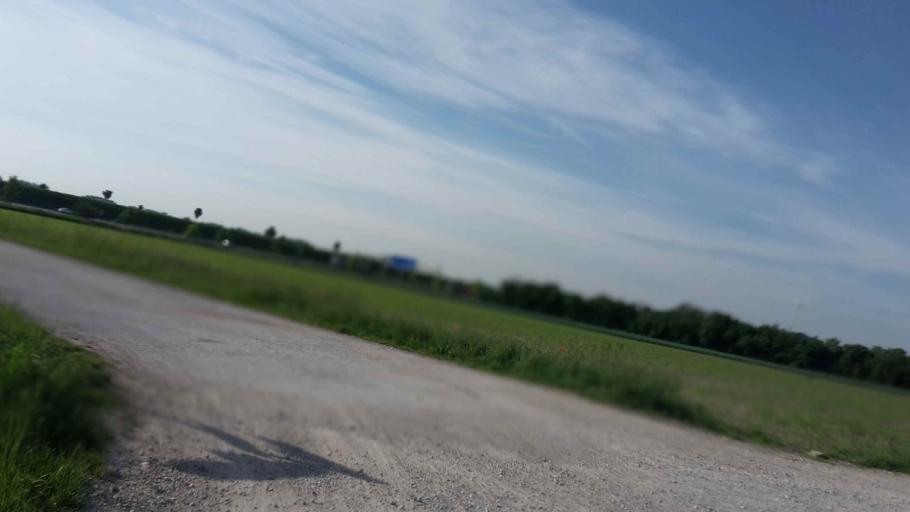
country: DE
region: Bavaria
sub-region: Upper Bavaria
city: Garching bei Munchen
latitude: 48.2341
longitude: 11.6326
